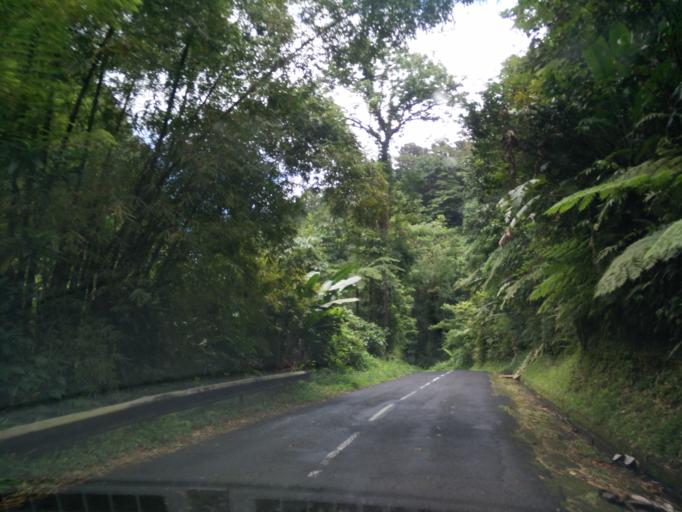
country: MQ
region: Martinique
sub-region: Martinique
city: Le Morne-Rouge
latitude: 14.7255
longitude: -61.1153
